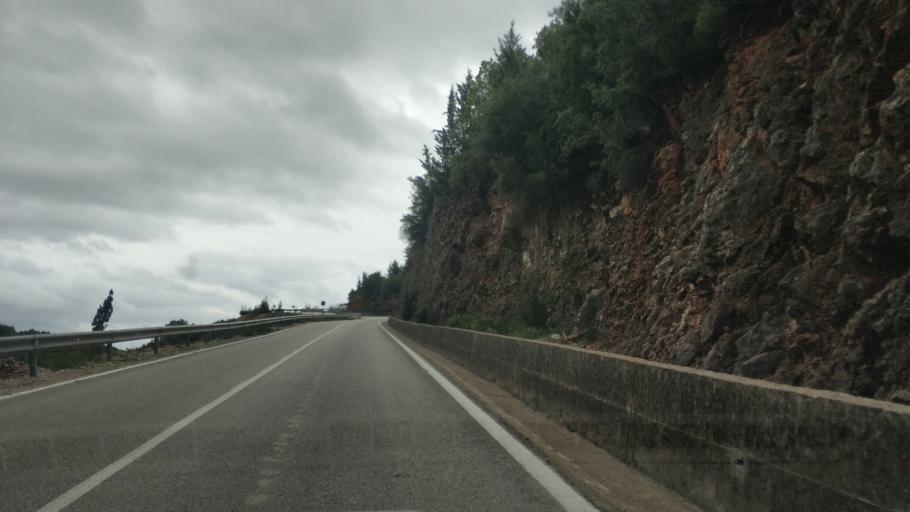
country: AL
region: Vlore
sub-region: Rrethi i Vlores
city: Vranisht
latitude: 40.1419
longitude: 19.6759
